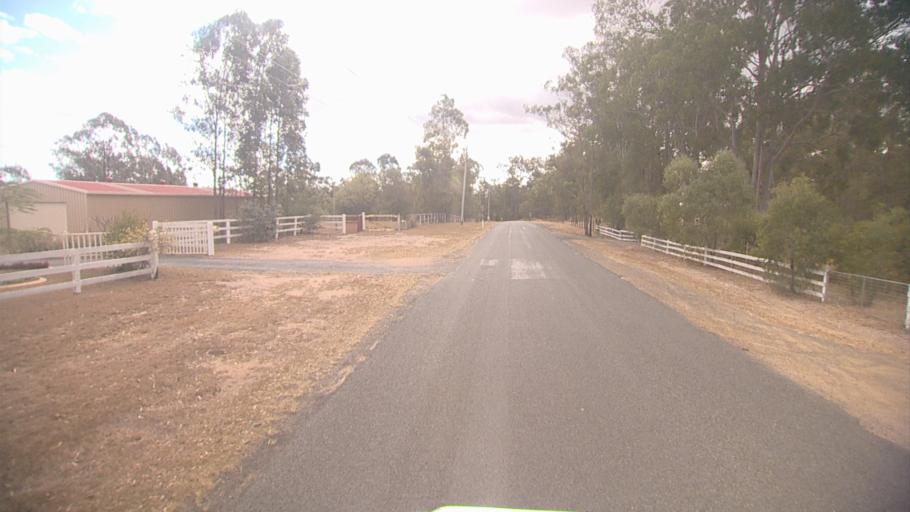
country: AU
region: Queensland
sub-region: Logan
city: Cedar Vale
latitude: -27.8773
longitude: 153.0275
